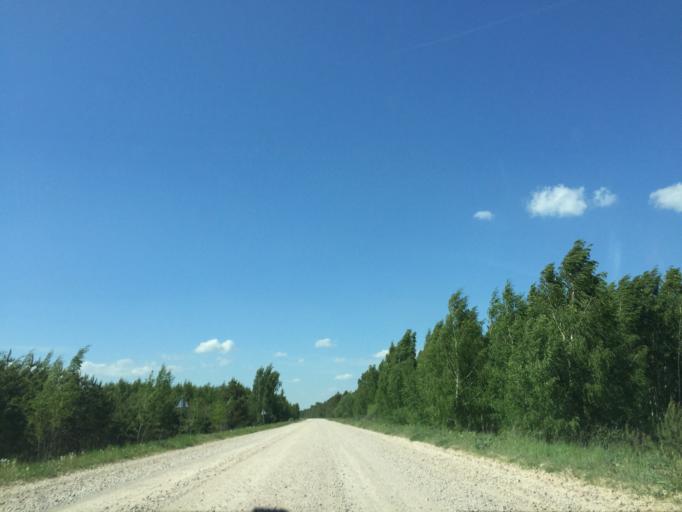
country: LV
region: Rundales
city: Pilsrundale
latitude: 56.5381
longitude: 23.9962
